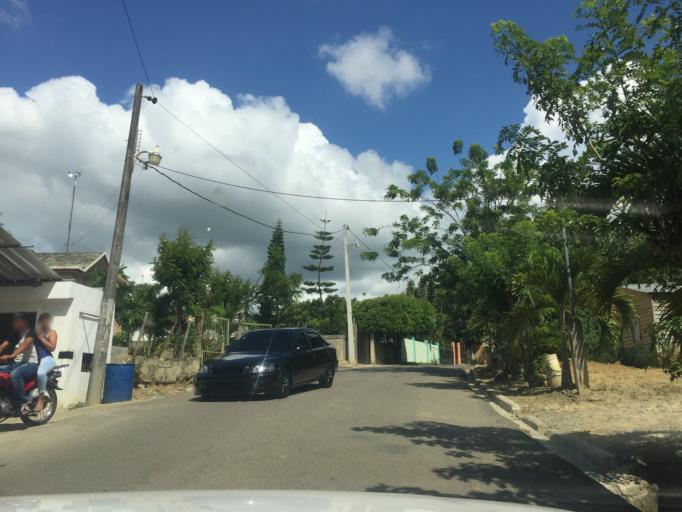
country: DO
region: La Vega
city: Rio Verde Arriba
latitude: 19.3575
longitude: -70.5913
